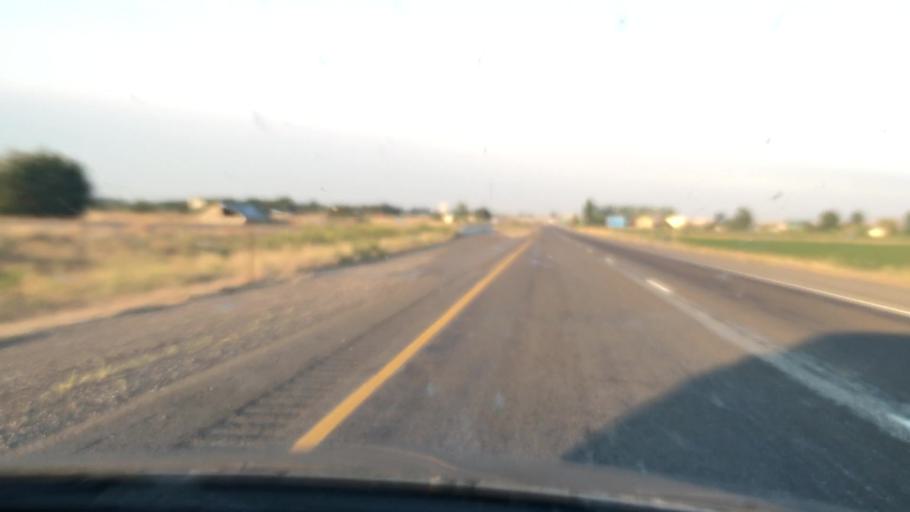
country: US
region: Idaho
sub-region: Minidoka County
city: Rupert
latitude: 42.5687
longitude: -113.6387
